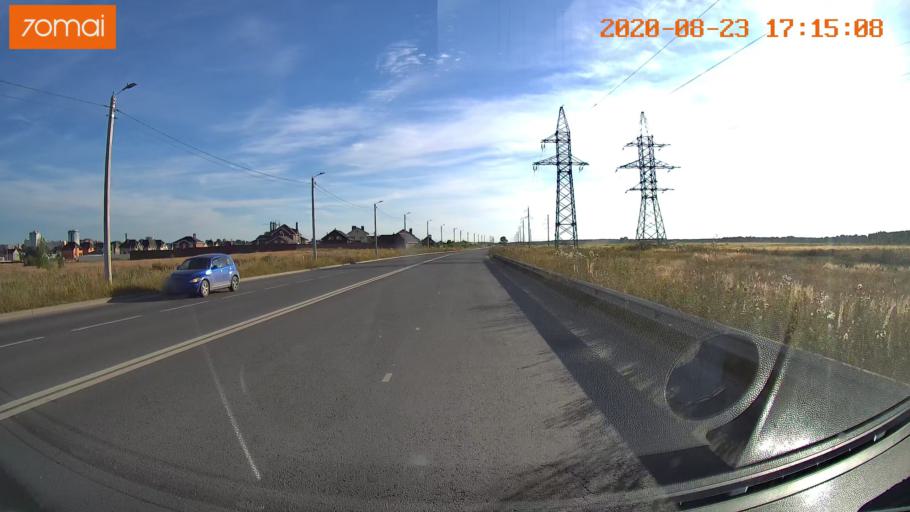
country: RU
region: Ivanovo
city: Novo-Talitsy
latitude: 57.0473
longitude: 40.9159
